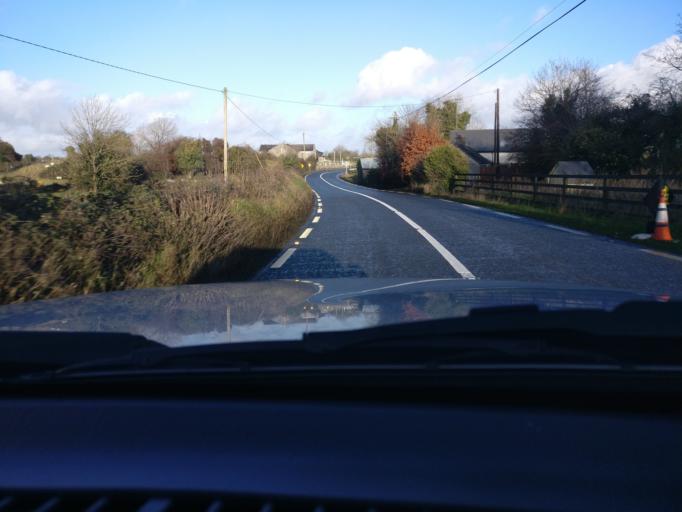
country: IE
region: Leinster
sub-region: An Iarmhi
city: Rathwire
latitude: 53.5659
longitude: -7.1936
